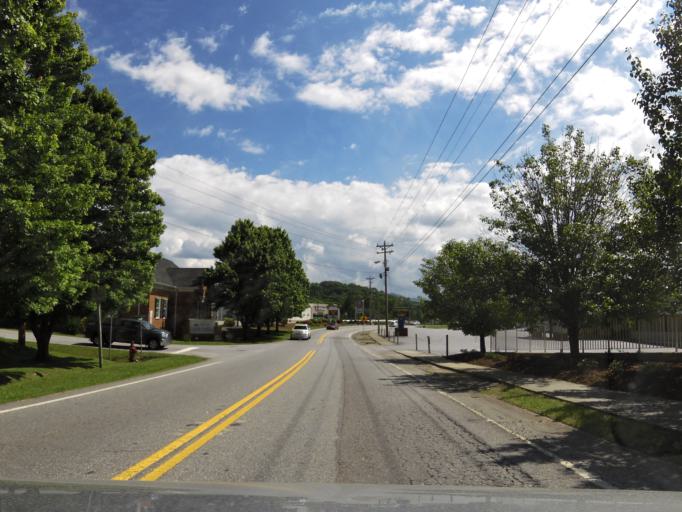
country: US
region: Georgia
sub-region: Union County
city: Blairsville
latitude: 34.8729
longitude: -83.9624
